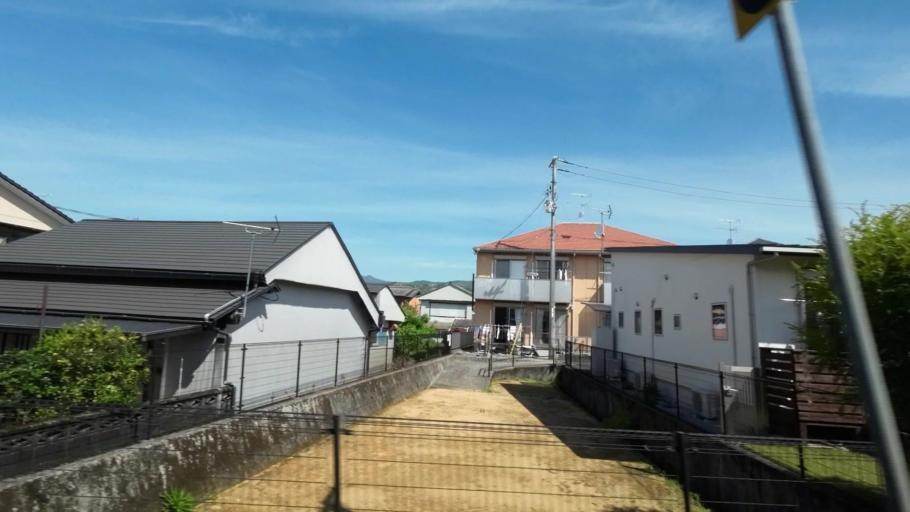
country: JP
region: Kochi
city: Kochi-shi
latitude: 33.6057
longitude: 133.6793
